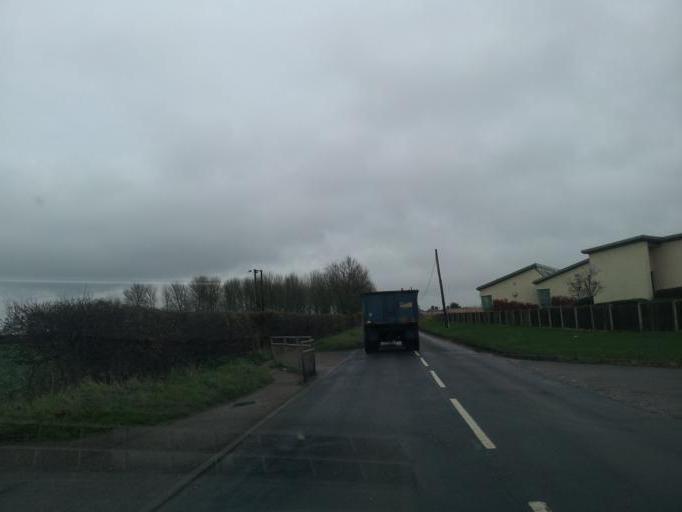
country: GB
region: England
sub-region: Norfolk
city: Martham
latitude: 52.7036
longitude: 1.6405
